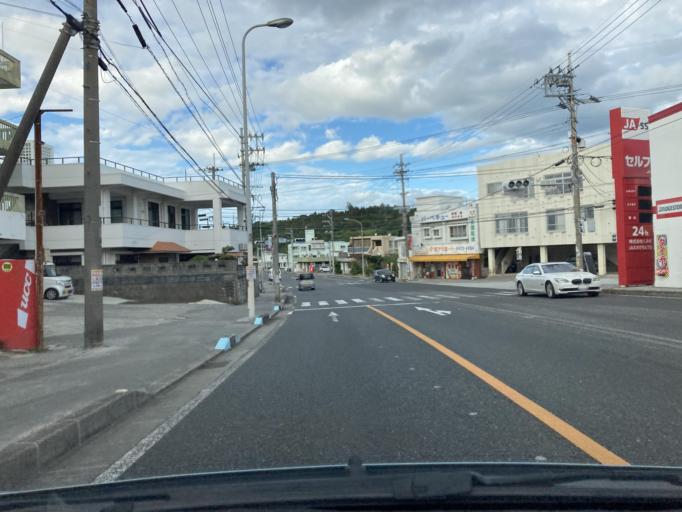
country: JP
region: Okinawa
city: Ishikawa
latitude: 26.3916
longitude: 127.8322
